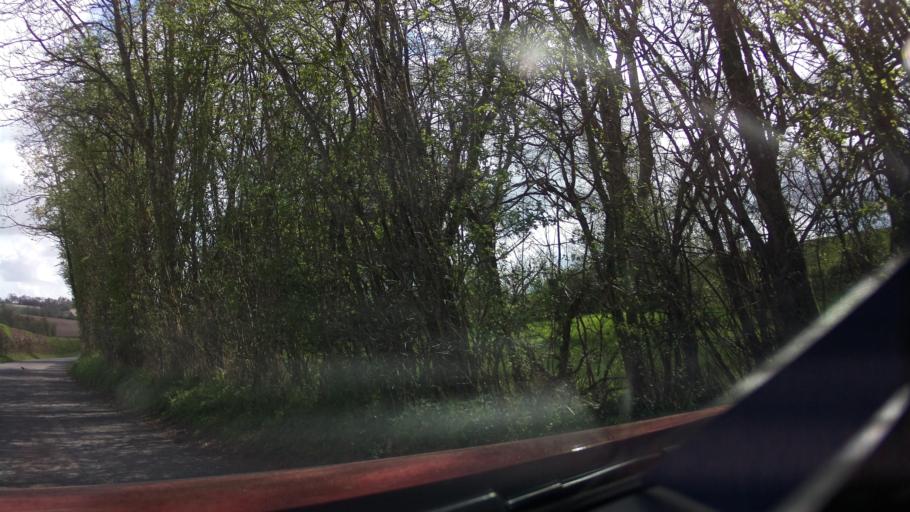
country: GB
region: England
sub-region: West Berkshire
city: Kintbury
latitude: 51.3253
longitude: -1.4662
